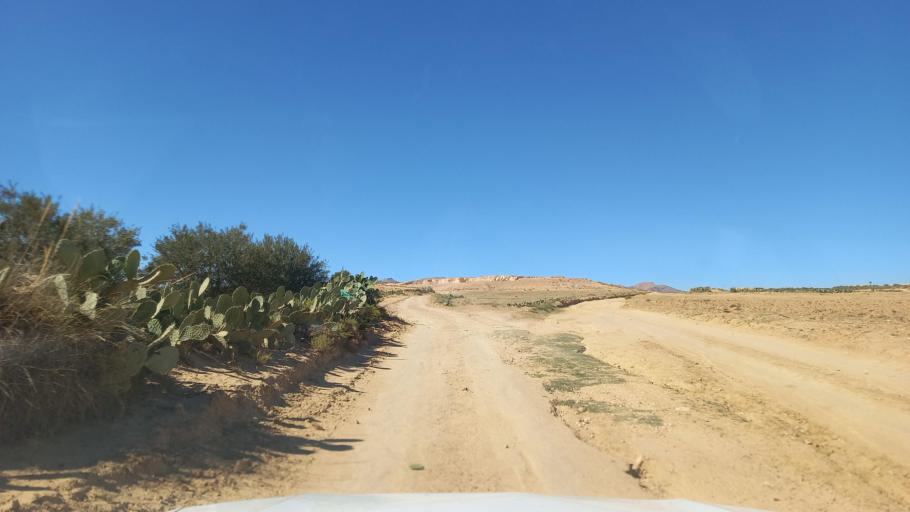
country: TN
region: Al Qasrayn
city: Sbiba
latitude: 35.3772
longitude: 9.0911
